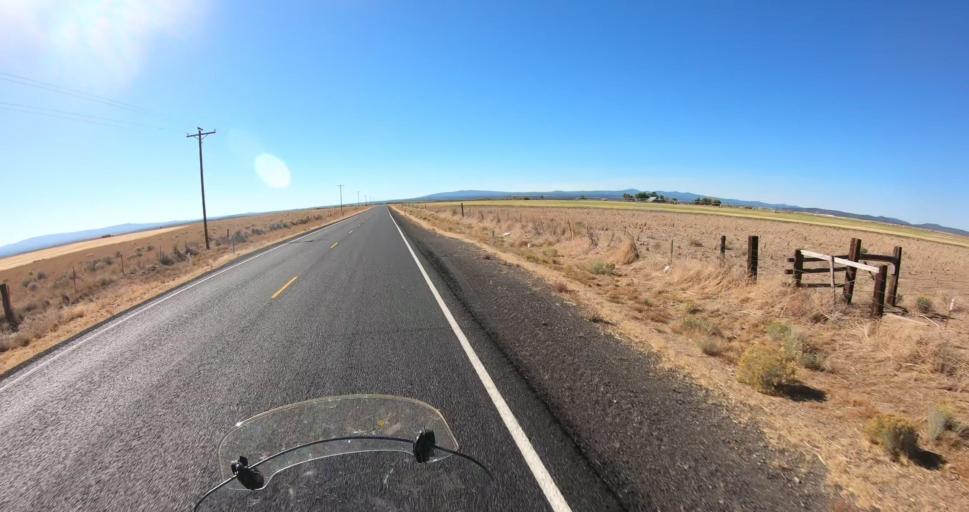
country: US
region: Oregon
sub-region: Deschutes County
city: La Pine
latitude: 43.1276
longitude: -120.9968
